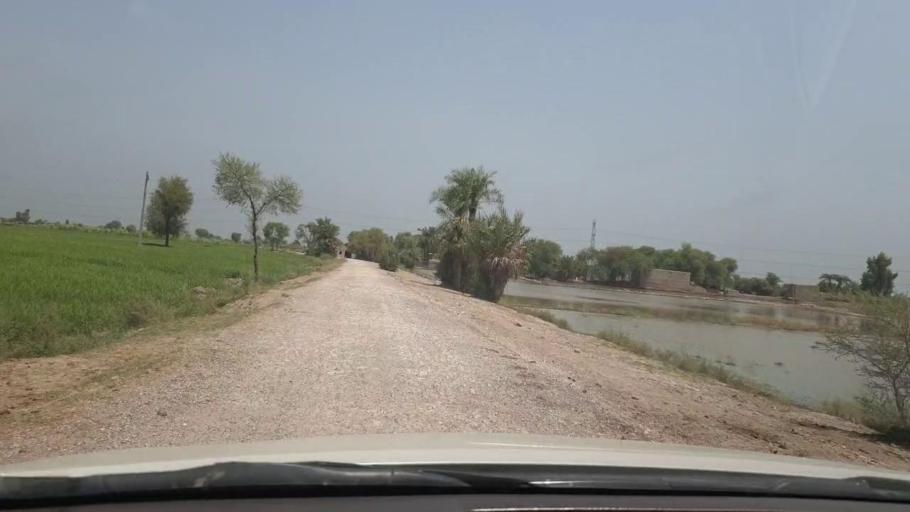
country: PK
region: Sindh
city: Shikarpur
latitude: 28.0227
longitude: 68.6465
